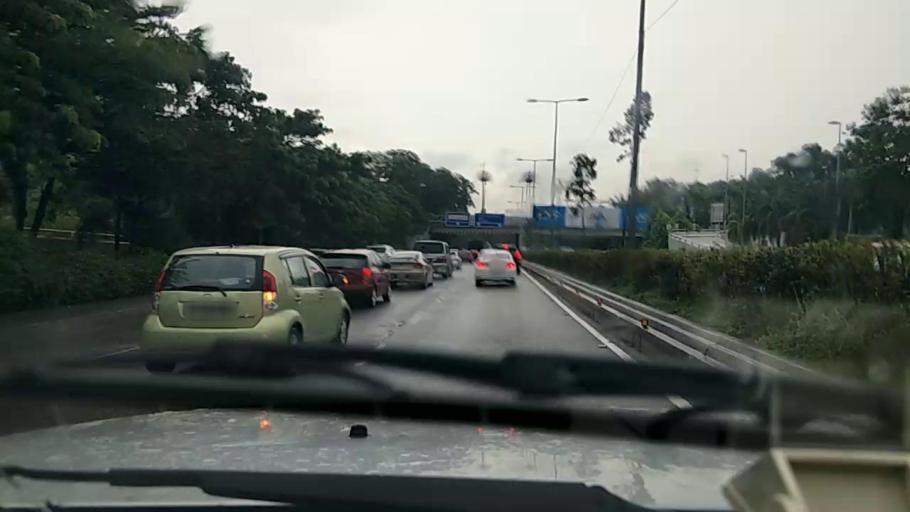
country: MY
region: Kuala Lumpur
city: Kuala Lumpur
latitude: 3.1232
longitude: 101.6816
